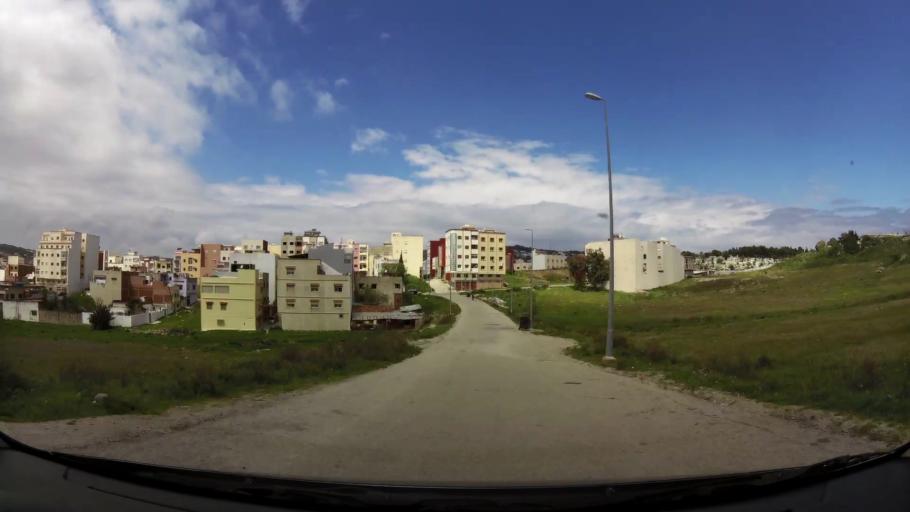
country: MA
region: Tanger-Tetouan
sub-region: Tanger-Assilah
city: Tangier
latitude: 35.7680
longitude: -5.8436
